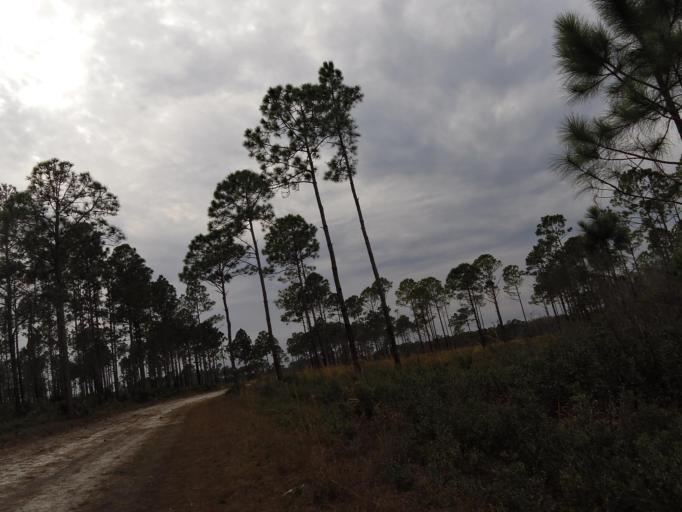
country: US
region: Florida
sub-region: Duval County
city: Atlantic Beach
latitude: 30.4709
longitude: -81.4962
